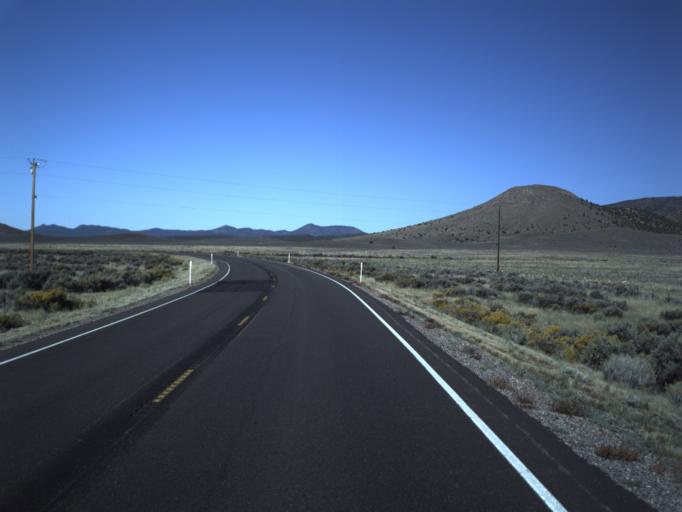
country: US
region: Utah
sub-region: Washington County
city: Enterprise
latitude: 37.8029
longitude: -113.9222
